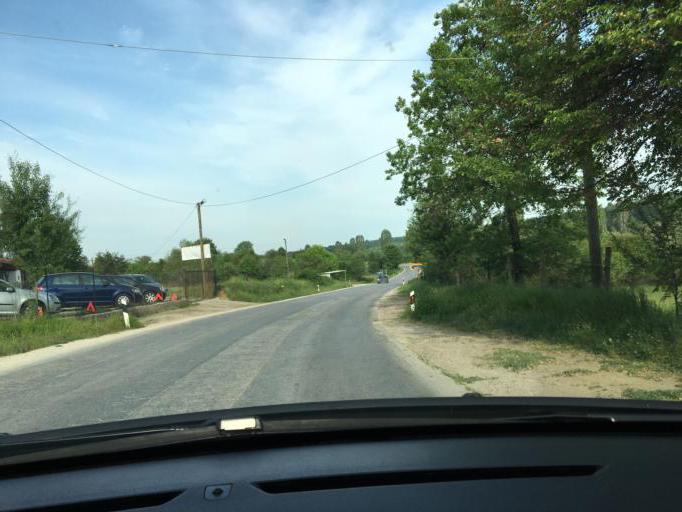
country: MK
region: Kriva Palanka
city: Kriva Palanka
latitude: 42.1785
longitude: 22.2655
